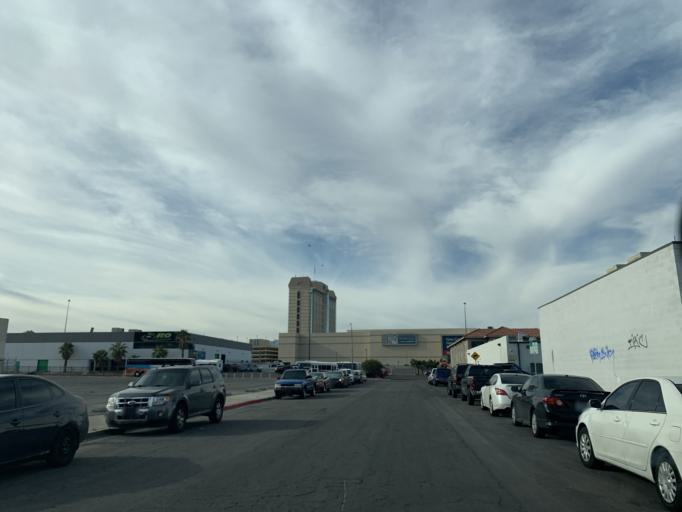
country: US
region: Nevada
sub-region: Clark County
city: Las Vegas
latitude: 36.1412
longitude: -115.1709
